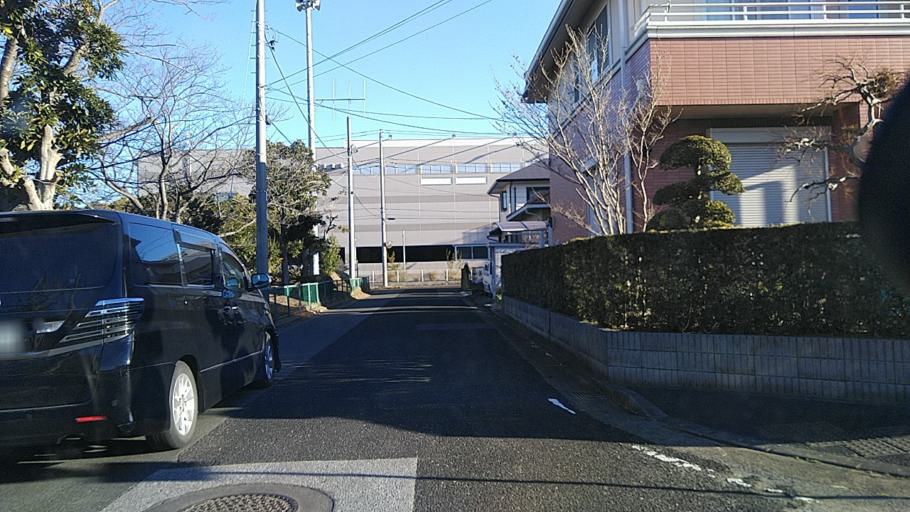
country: JP
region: Chiba
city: Kimitsu
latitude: 35.3333
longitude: 139.8903
